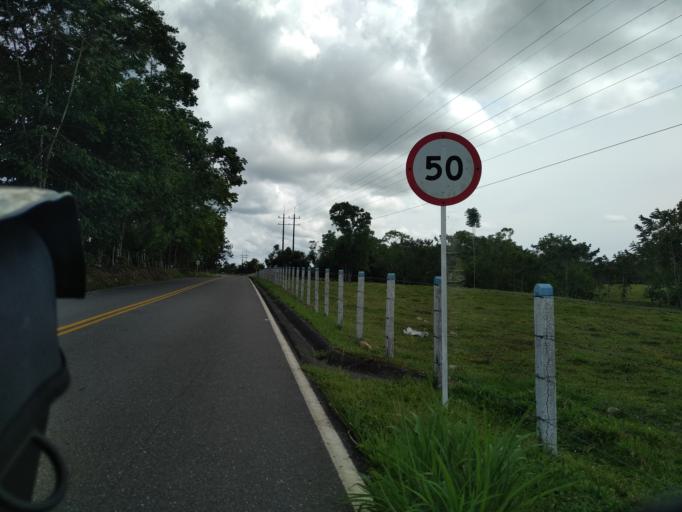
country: CO
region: Santander
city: Cimitarra
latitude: 6.4737
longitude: -74.0312
